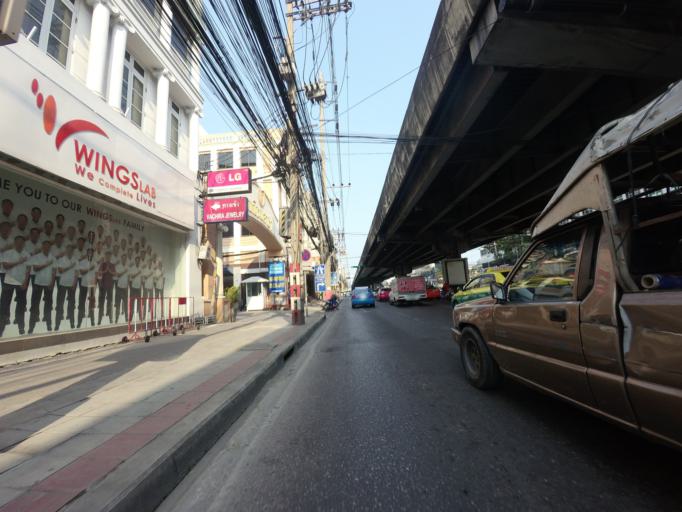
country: TH
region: Bangkok
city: Din Daeng
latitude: 13.7559
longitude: 100.5691
